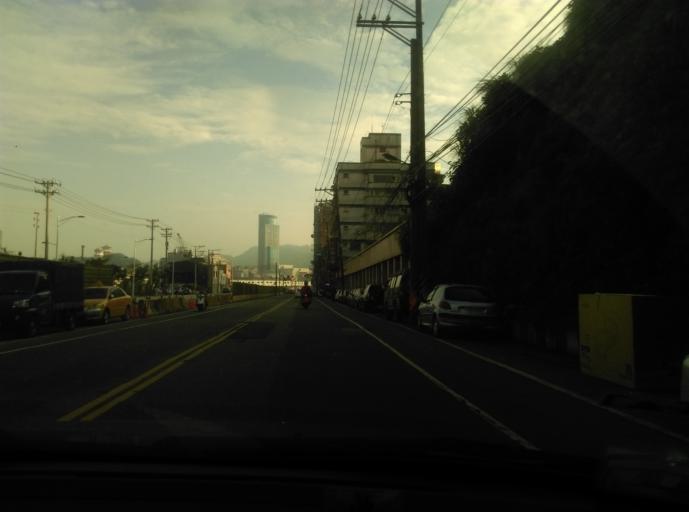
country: TW
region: Taiwan
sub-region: Keelung
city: Keelung
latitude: 25.1399
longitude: 121.7398
